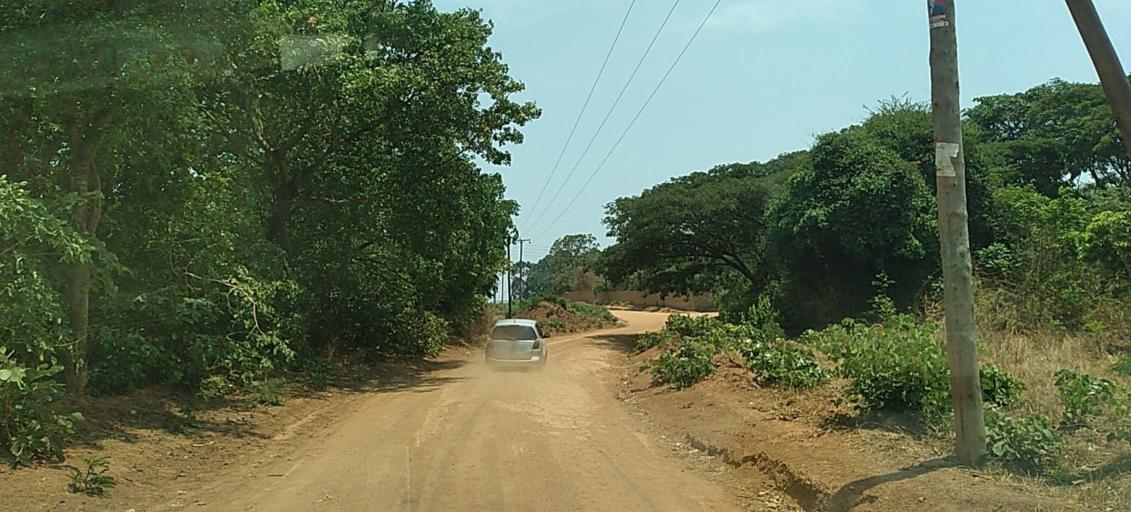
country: ZM
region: Copperbelt
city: Ndola
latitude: -13.0019
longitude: 28.7415
